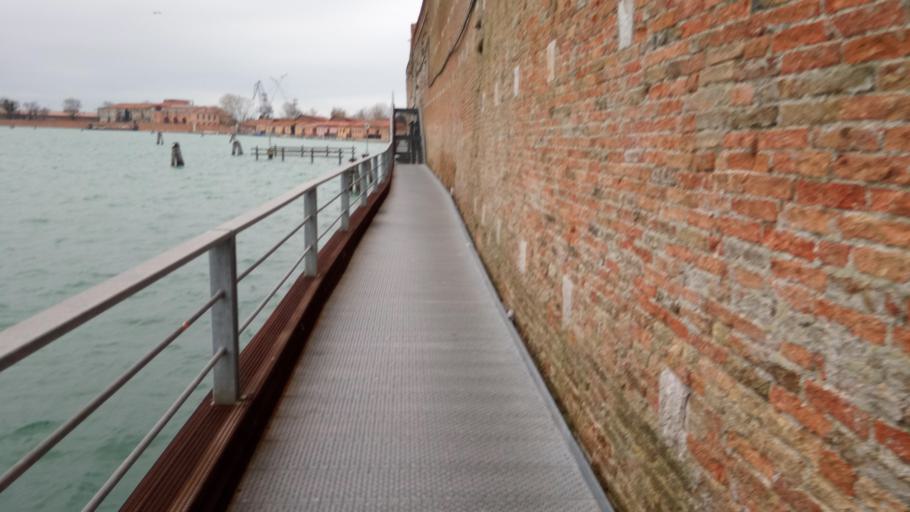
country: IT
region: Veneto
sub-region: Provincia di Venezia
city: Venice
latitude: 45.4387
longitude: 12.3514
